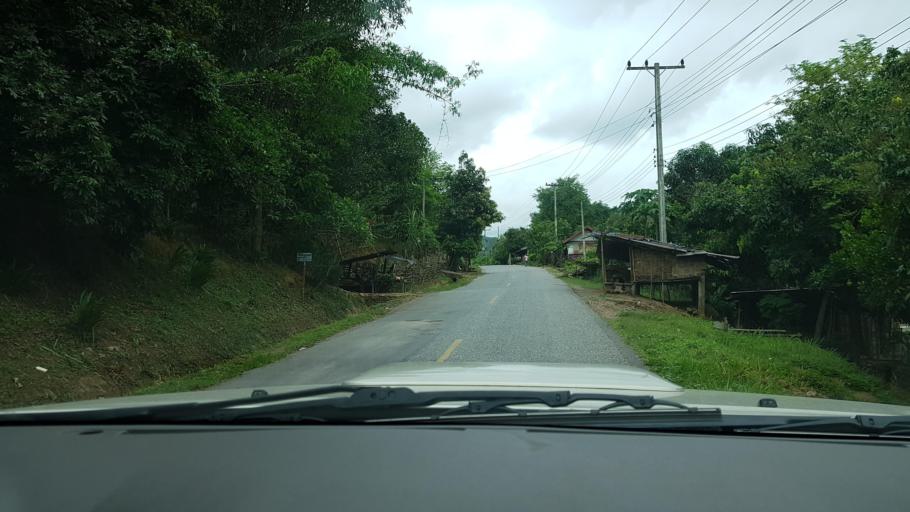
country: LA
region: Loungnamtha
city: Muang Nale
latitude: 20.3845
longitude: 101.7415
